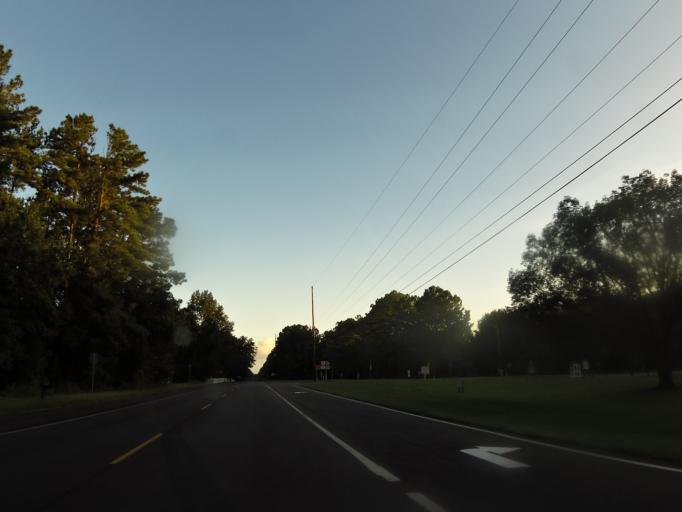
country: US
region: Georgia
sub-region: Camden County
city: Woodbine
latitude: 31.0323
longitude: -81.7305
